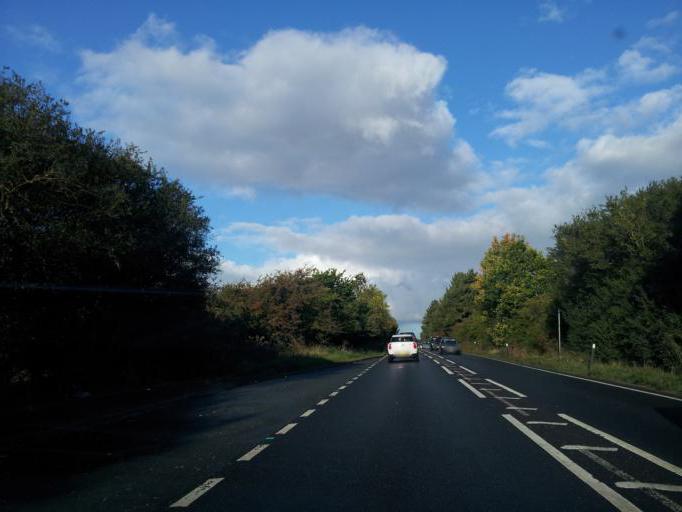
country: GB
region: England
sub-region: Norfolk
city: Mattishall
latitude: 52.6650
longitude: 1.1075
